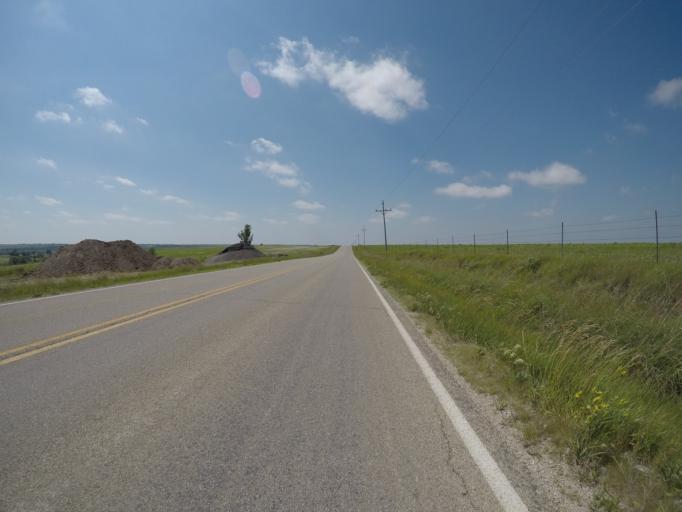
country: US
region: Kansas
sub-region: Pottawatomie County
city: Westmoreland
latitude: 39.3880
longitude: -96.4266
